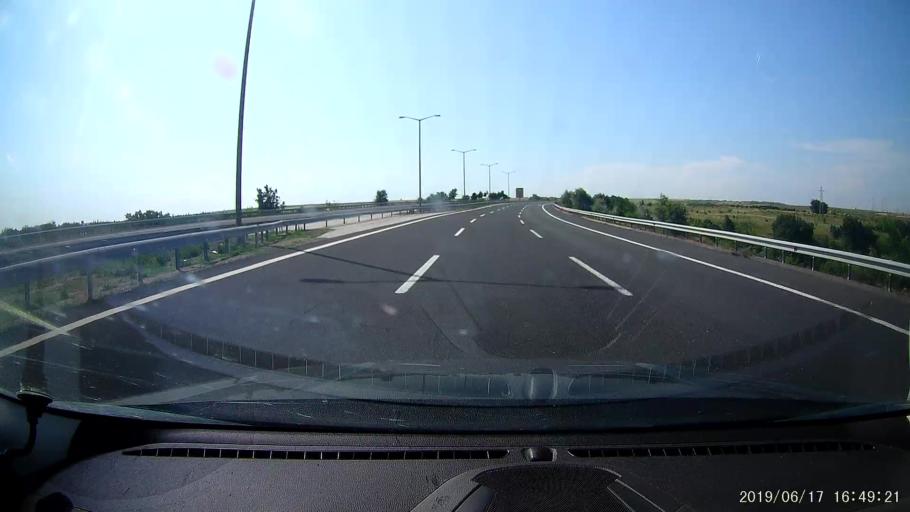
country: TR
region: Kirklareli
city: Babaeski
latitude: 41.5071
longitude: 27.1144
